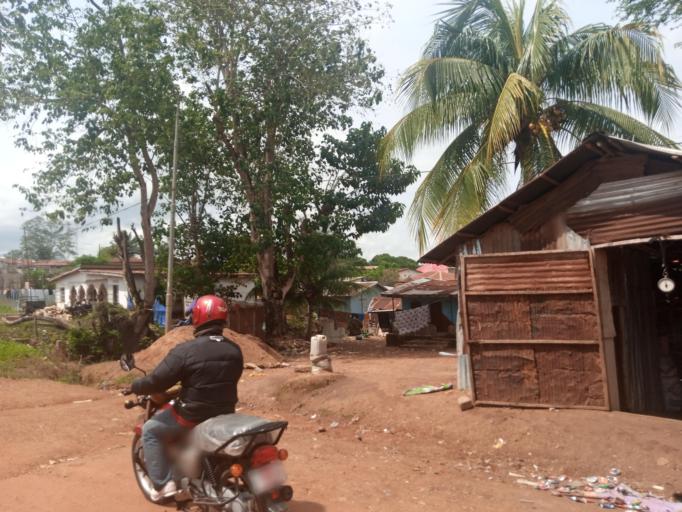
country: SL
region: Southern Province
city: Bo
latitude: 7.9667
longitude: -11.7440
